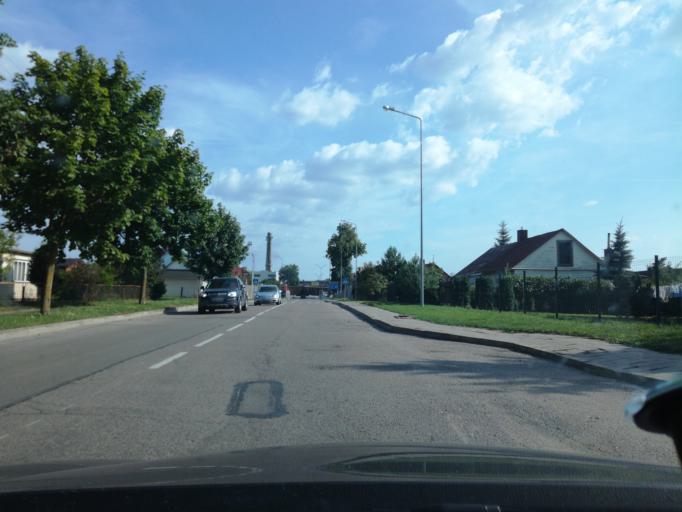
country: LT
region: Marijampoles apskritis
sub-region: Marijampole Municipality
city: Marijampole
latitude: 54.5409
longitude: 23.3497
